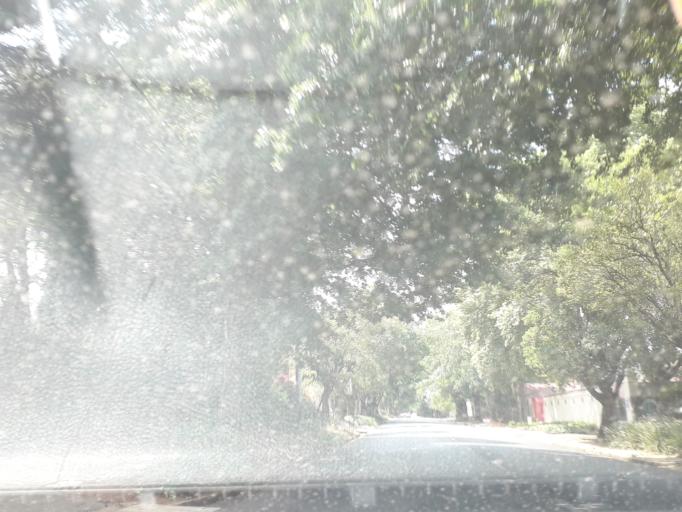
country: ZA
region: Gauteng
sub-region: City of Johannesburg Metropolitan Municipality
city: Johannesburg
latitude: -26.1586
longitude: 28.0172
